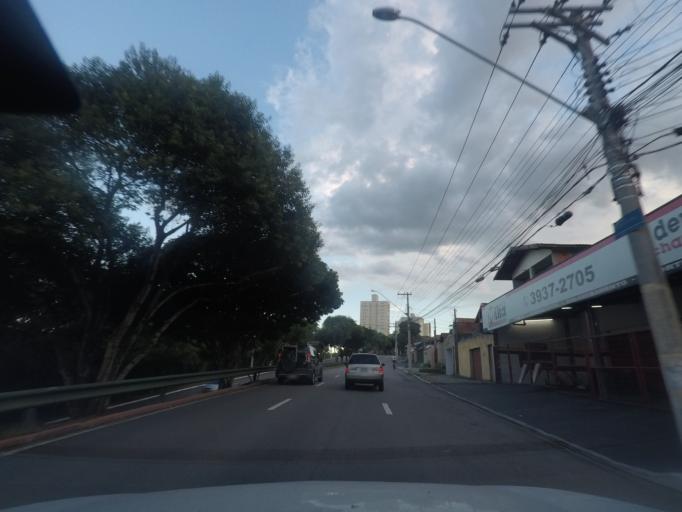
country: BR
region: Sao Paulo
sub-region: Sao Jose Dos Campos
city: Sao Jose dos Campos
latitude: -23.2235
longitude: -45.8820
